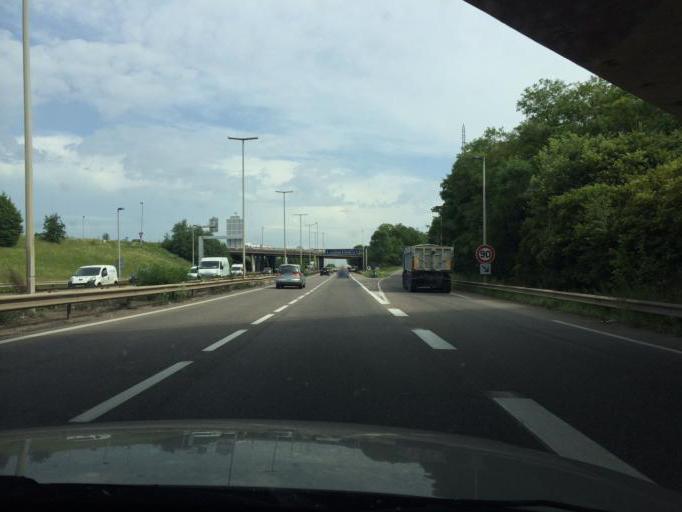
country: FR
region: Lorraine
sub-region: Departement de Meurthe-et-Moselle
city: Ludres
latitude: 48.6279
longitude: 6.1817
